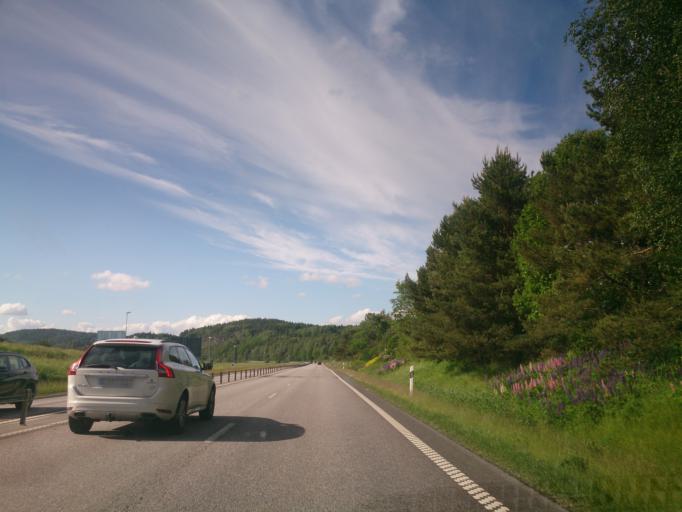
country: SE
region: OEstergoetland
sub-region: Norrkopings Kommun
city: Jursla
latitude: 58.6615
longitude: 16.1686
